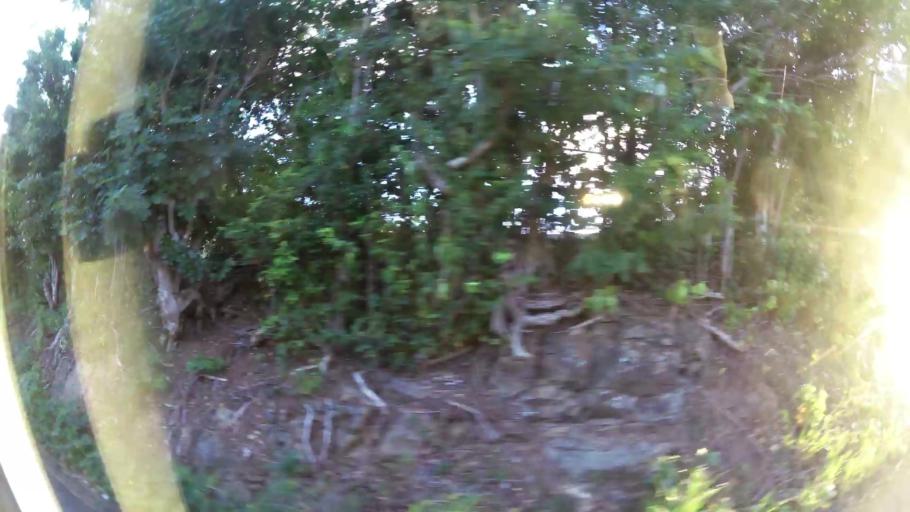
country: LC
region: Gros-Islet
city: Gros Islet
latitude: 14.0720
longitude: -60.9443
